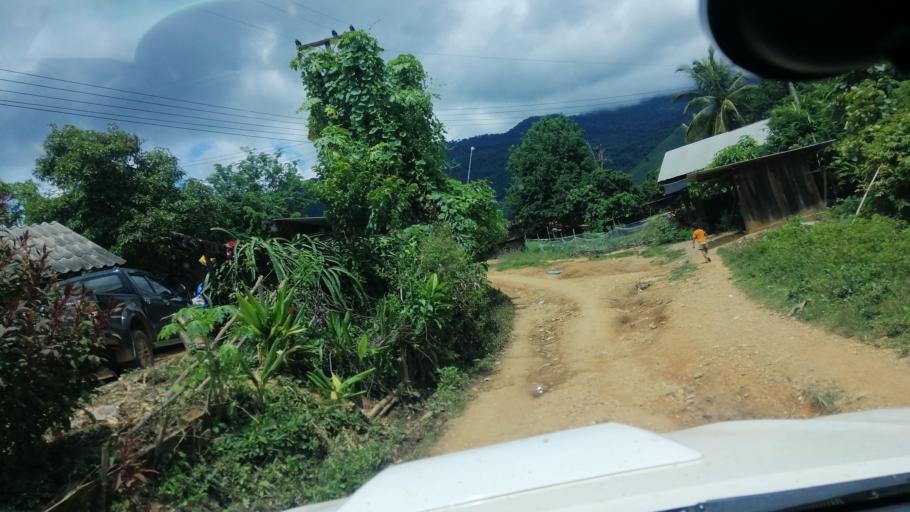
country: TH
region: Phayao
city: Phu Sang
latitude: 19.7444
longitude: 100.4306
